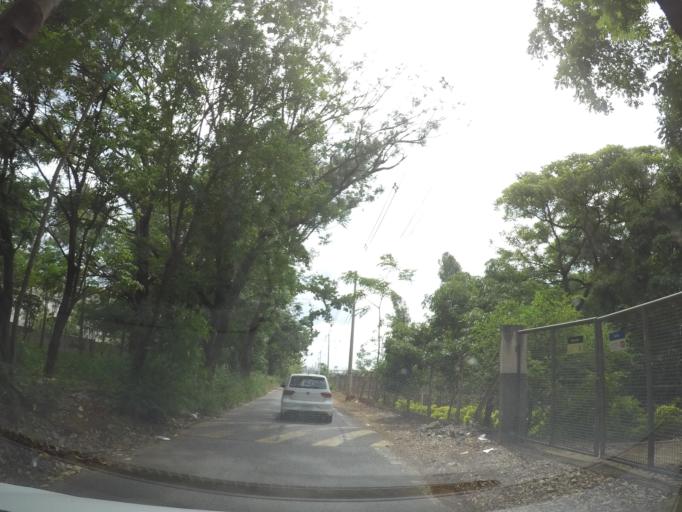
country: BR
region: Sao Paulo
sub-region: Sumare
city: Sumare
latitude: -22.7996
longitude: -47.2280
